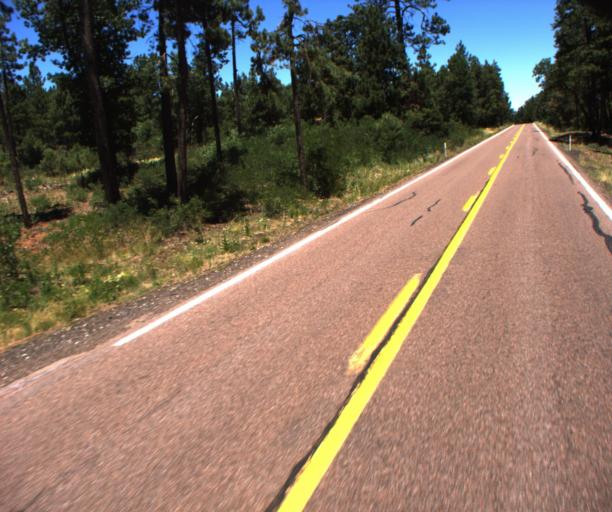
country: US
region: Arizona
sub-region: Gila County
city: Pine
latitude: 34.4687
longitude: -111.3822
